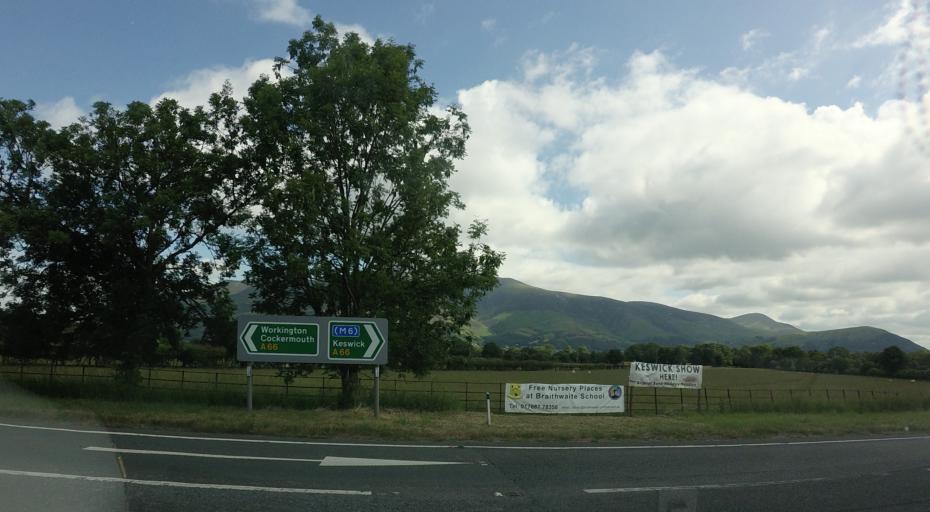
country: GB
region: England
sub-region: Cumbria
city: Keswick
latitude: 54.6024
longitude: -3.1846
